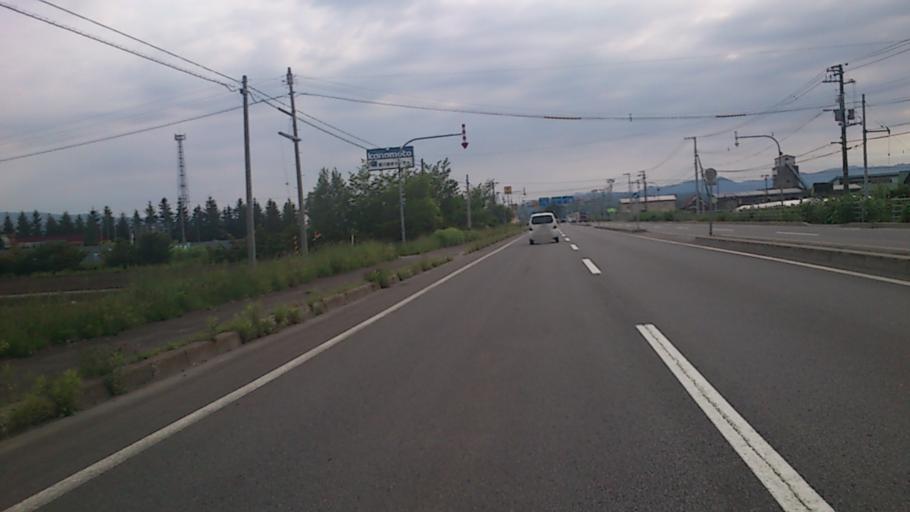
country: JP
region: Hokkaido
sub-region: Asahikawa-shi
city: Asahikawa
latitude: 43.8533
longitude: 142.5025
